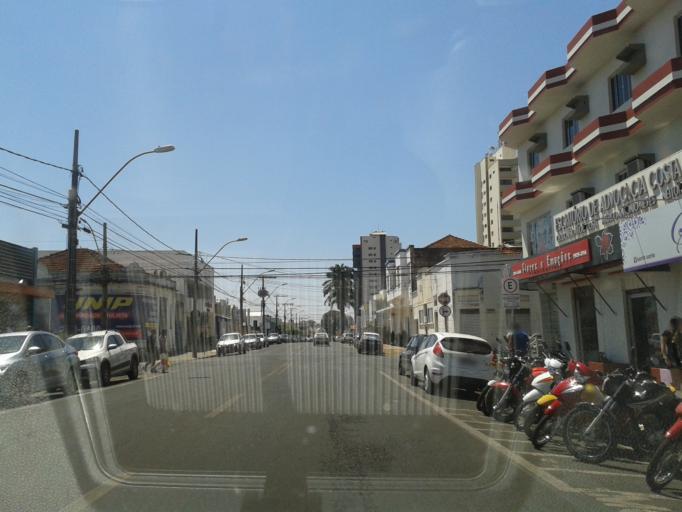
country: BR
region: Minas Gerais
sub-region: Araguari
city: Araguari
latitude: -18.6518
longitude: -48.1907
